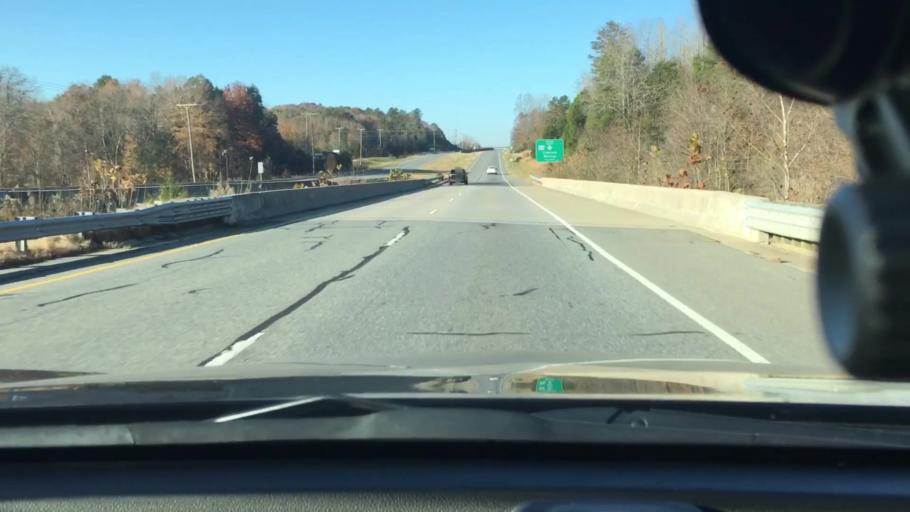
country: US
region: North Carolina
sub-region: Cabarrus County
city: Concord
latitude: 35.3763
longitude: -80.5365
